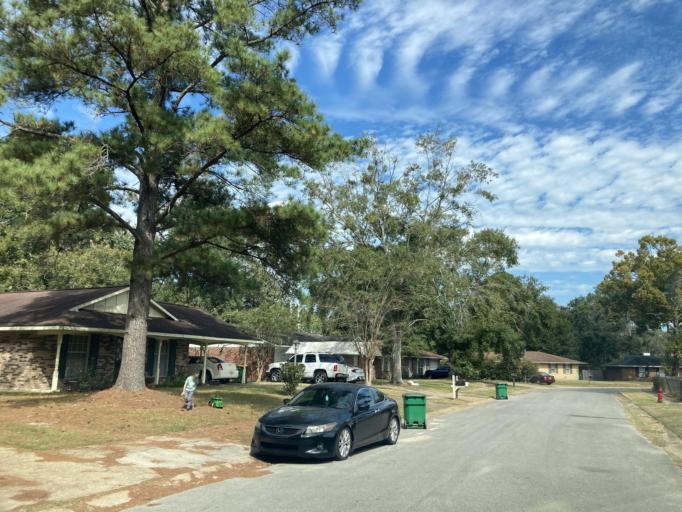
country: US
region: Mississippi
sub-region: Jackson County
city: Saint Martin
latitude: 30.4490
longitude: -88.8760
